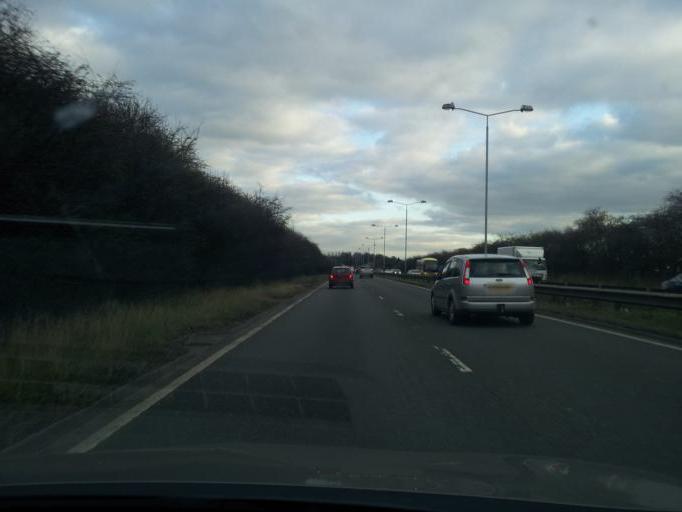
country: GB
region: England
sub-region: Nottinghamshire
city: Ruddington
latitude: 52.9111
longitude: -1.1544
